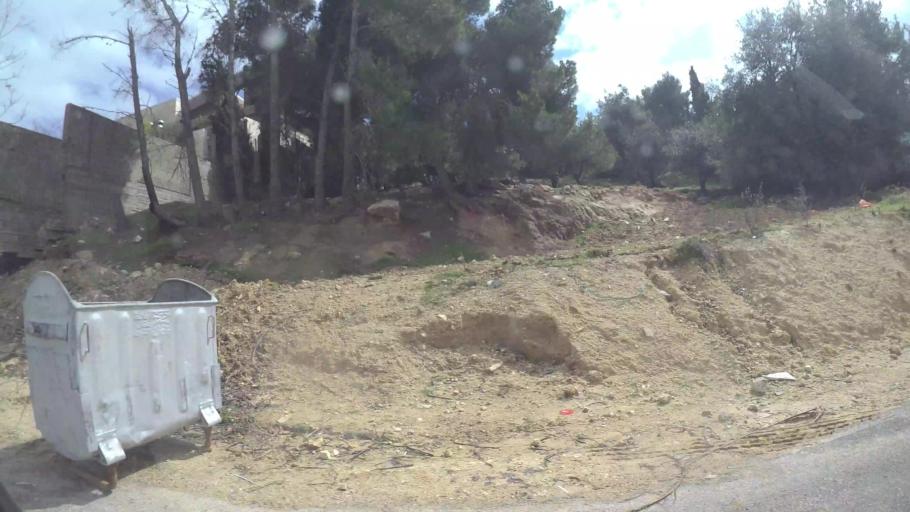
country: JO
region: Amman
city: Al Jubayhah
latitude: 32.0347
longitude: 35.8164
